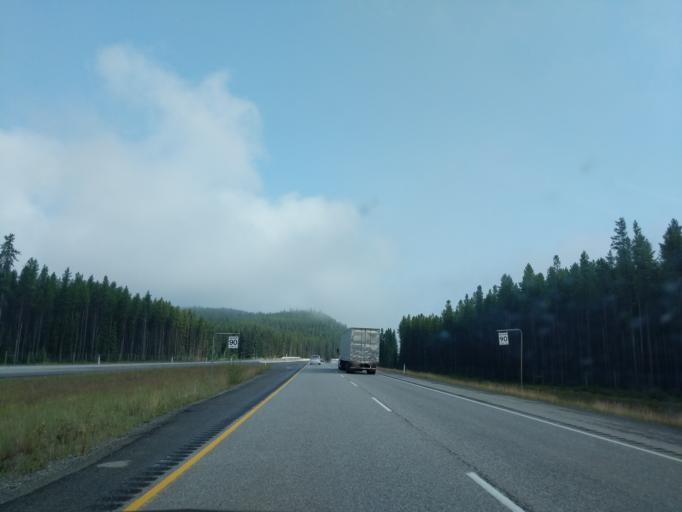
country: CA
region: Alberta
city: Lake Louise
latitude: 51.3064
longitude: -116.0208
